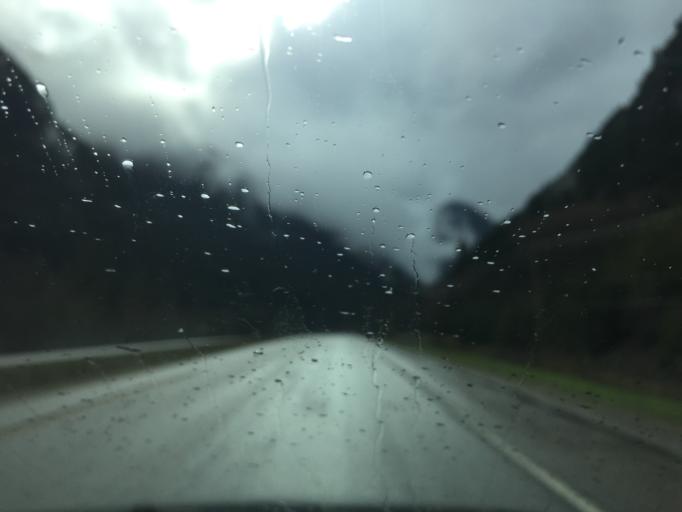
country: CA
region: British Columbia
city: Hope
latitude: 49.4472
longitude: -121.2711
